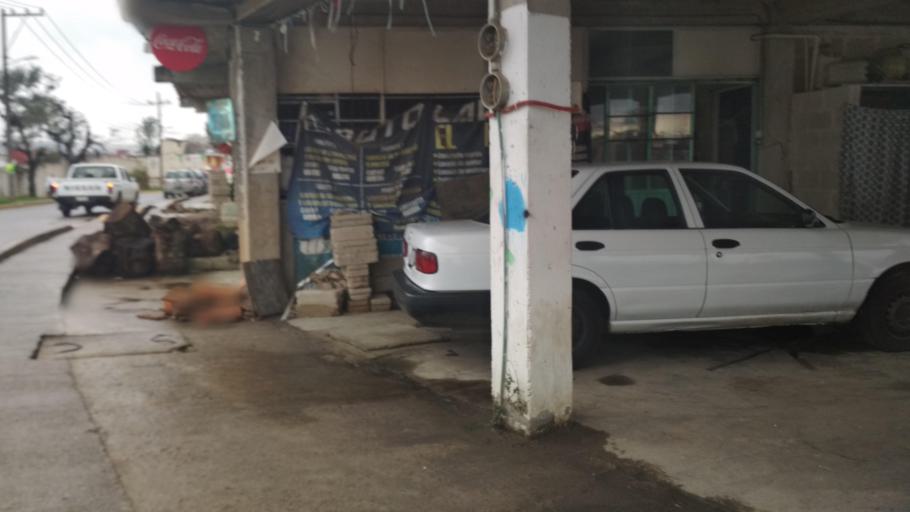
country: MX
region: Veracruz
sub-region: Emiliano Zapata
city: Las Trancas
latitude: 19.5045
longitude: -96.8678
